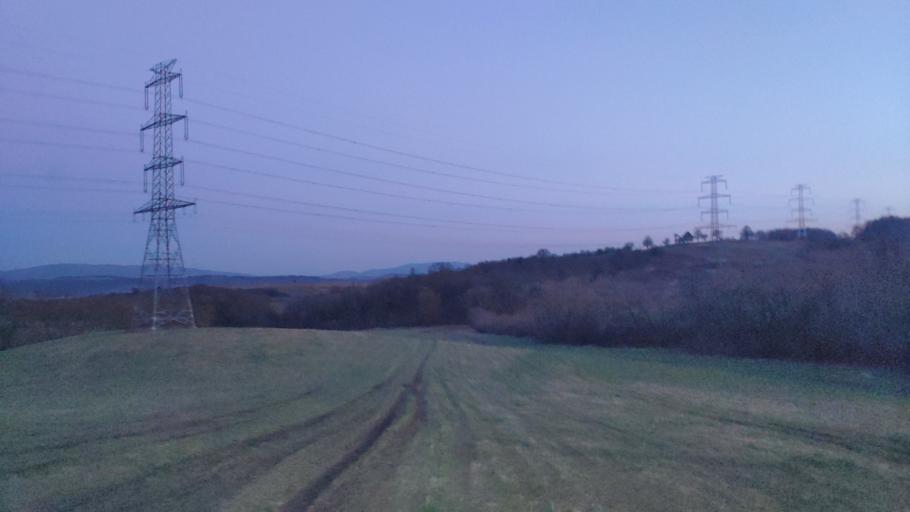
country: SK
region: Kosicky
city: Kosice
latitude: 48.8231
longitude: 21.2686
